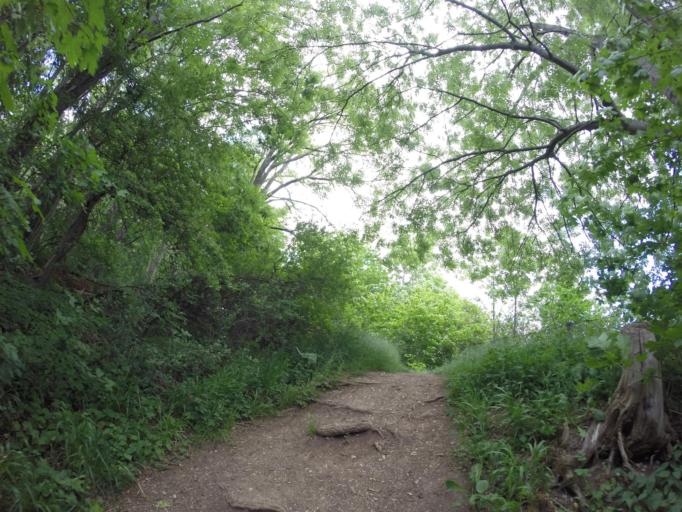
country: DE
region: Thuringia
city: Sulza
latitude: 50.8891
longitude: 11.6237
